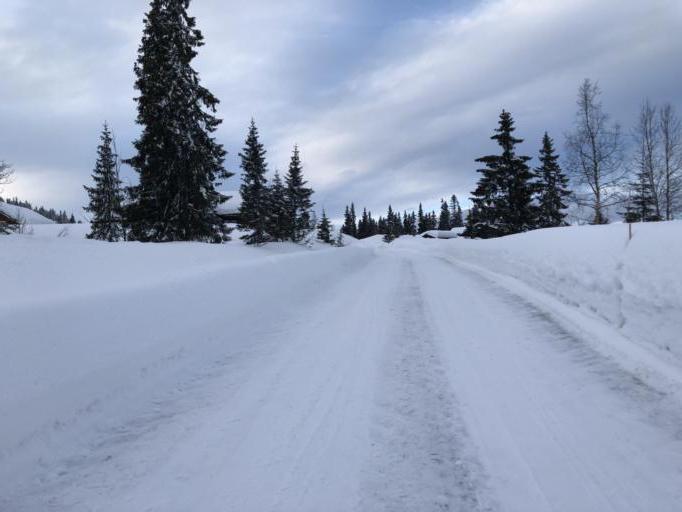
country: NO
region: Oppland
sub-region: Gausdal
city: Segalstad bru
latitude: 61.3289
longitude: 10.0536
